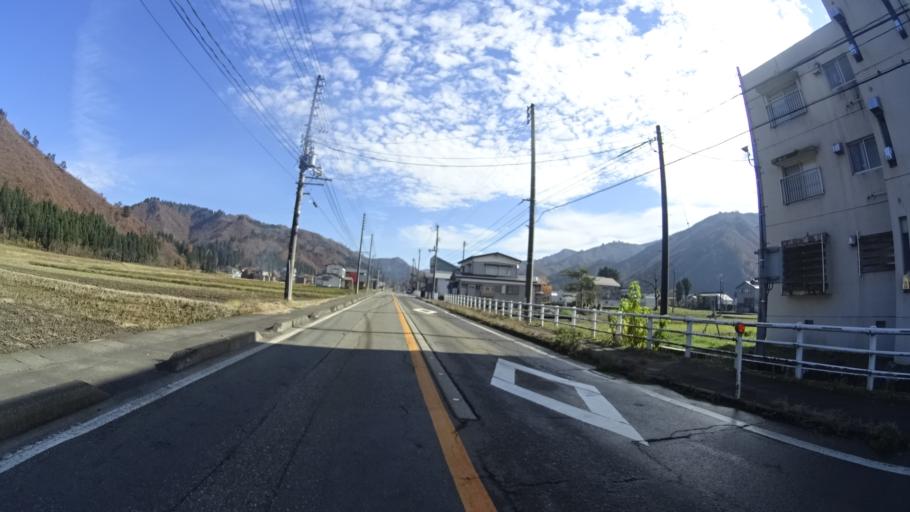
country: JP
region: Niigata
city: Muikamachi
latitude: 37.2274
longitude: 138.9971
